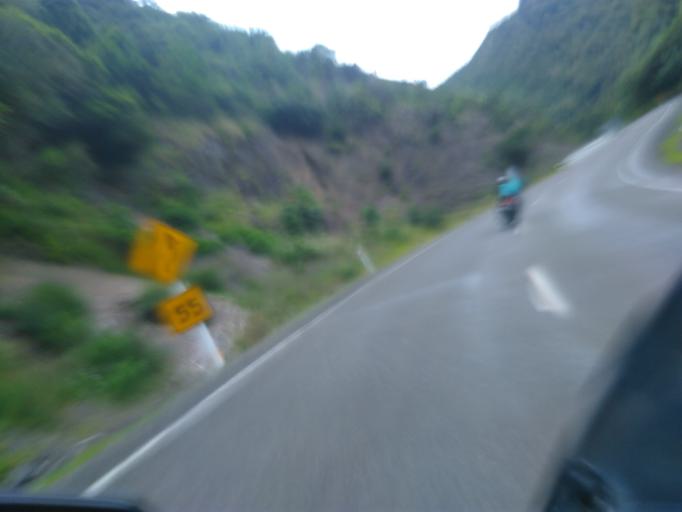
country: NZ
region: Bay of Plenty
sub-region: Opotiki District
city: Opotiki
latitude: -38.3065
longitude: 177.3965
